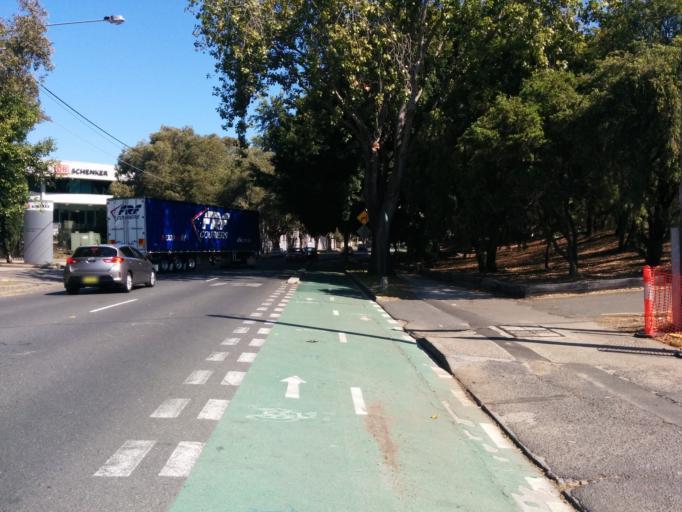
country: AU
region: New South Wales
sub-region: City of Sydney
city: Alexandria
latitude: -33.9081
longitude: 151.1974
